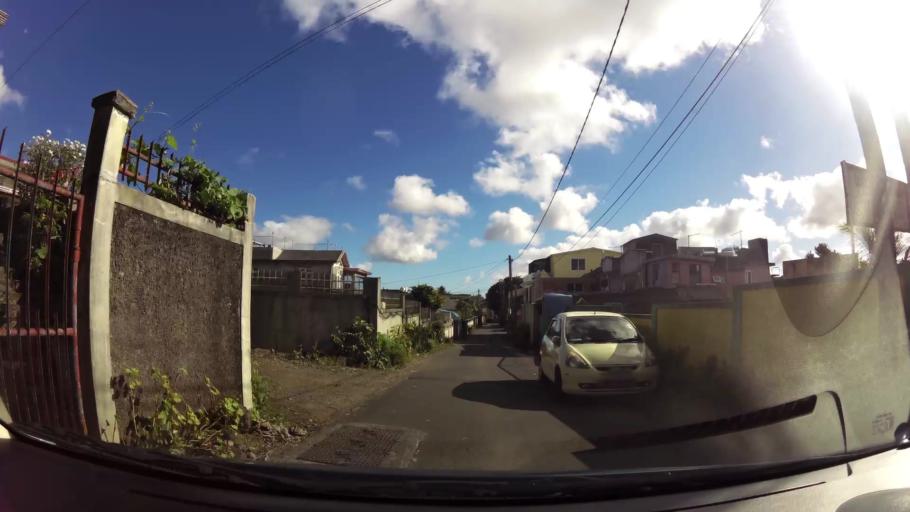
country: MU
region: Plaines Wilhems
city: Curepipe
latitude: -20.3011
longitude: 57.5179
